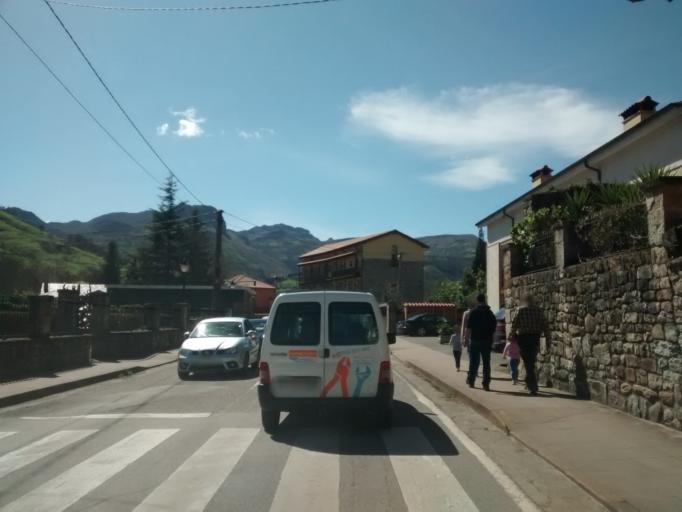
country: ES
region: Cantabria
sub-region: Provincia de Cantabria
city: Lierganes
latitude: 43.3401
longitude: -3.7445
